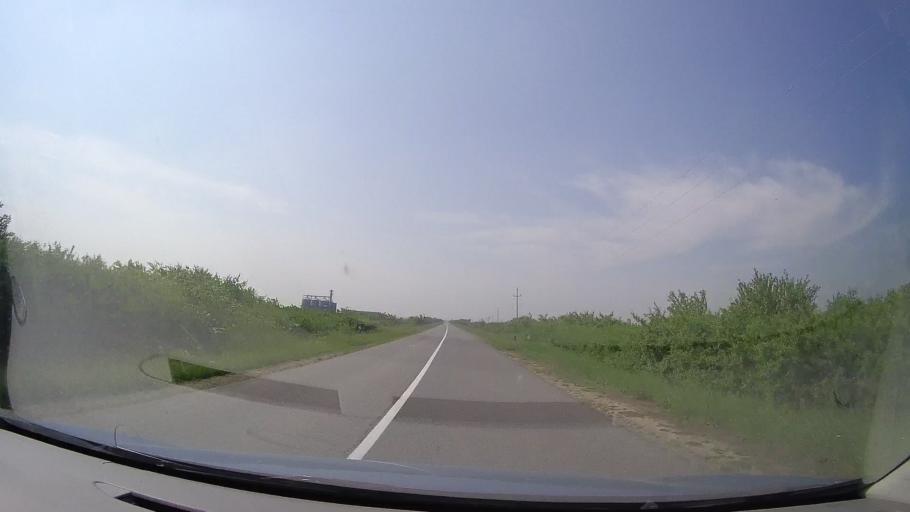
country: RS
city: Jarkovac
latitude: 45.2580
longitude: 20.7637
